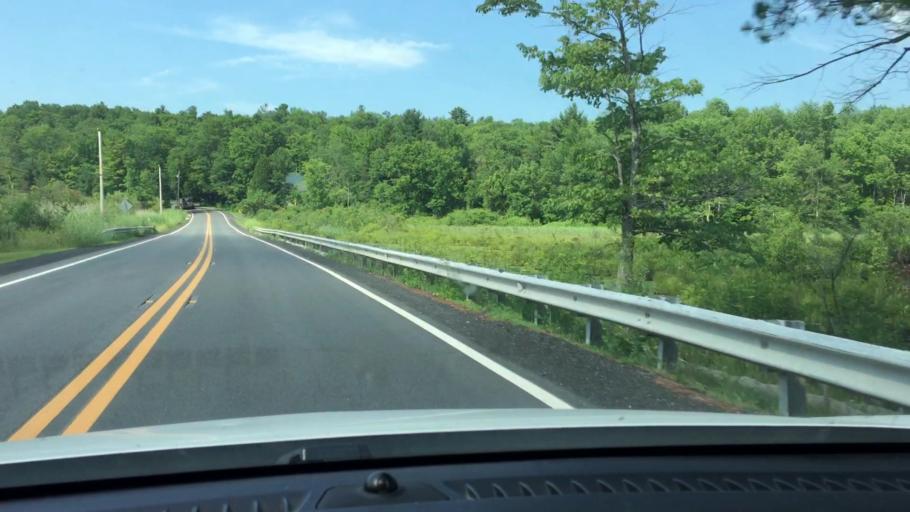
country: US
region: Massachusetts
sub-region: Berkshire County
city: Otis
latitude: 42.1984
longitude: -73.1150
